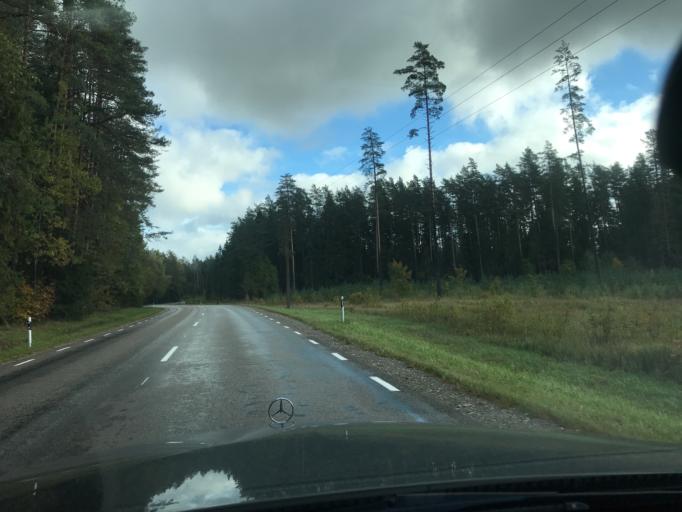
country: EE
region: Valgamaa
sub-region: Torva linn
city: Torva
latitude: 58.0098
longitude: 26.1073
